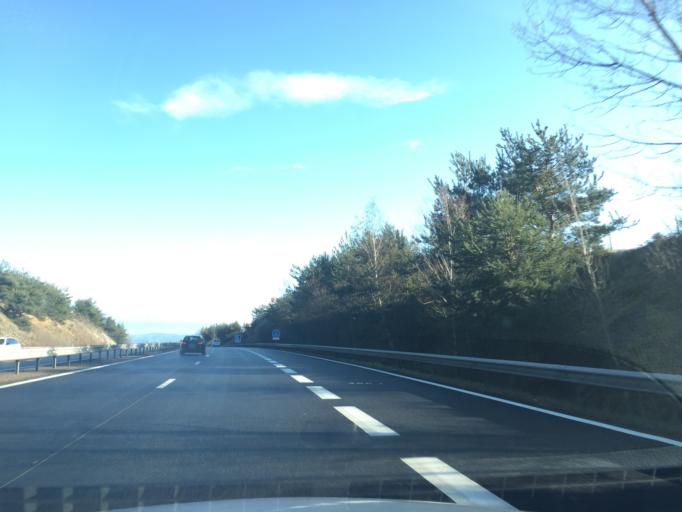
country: FR
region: Rhone-Alpes
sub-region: Departement de la Loire
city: Saint-Germain-Laval
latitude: 45.8706
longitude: 3.9287
